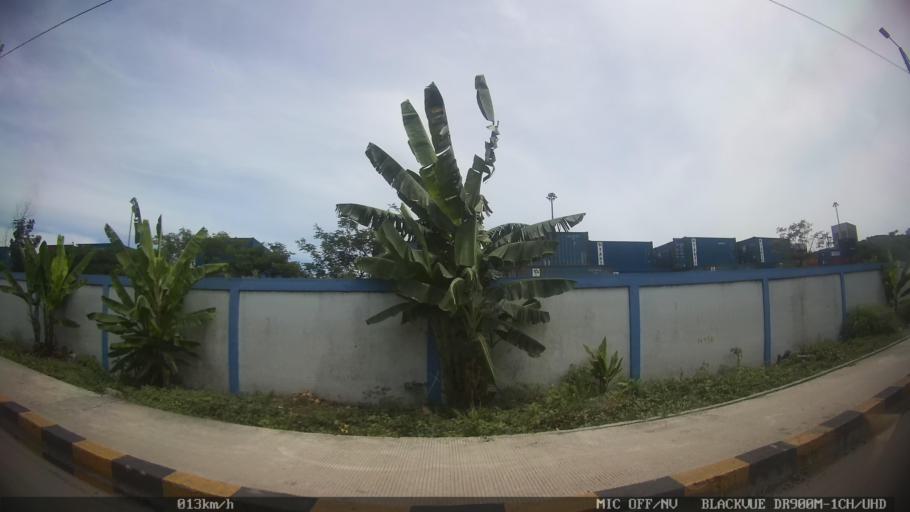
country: ID
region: North Sumatra
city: Belawan
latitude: 3.7814
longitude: 98.6951
